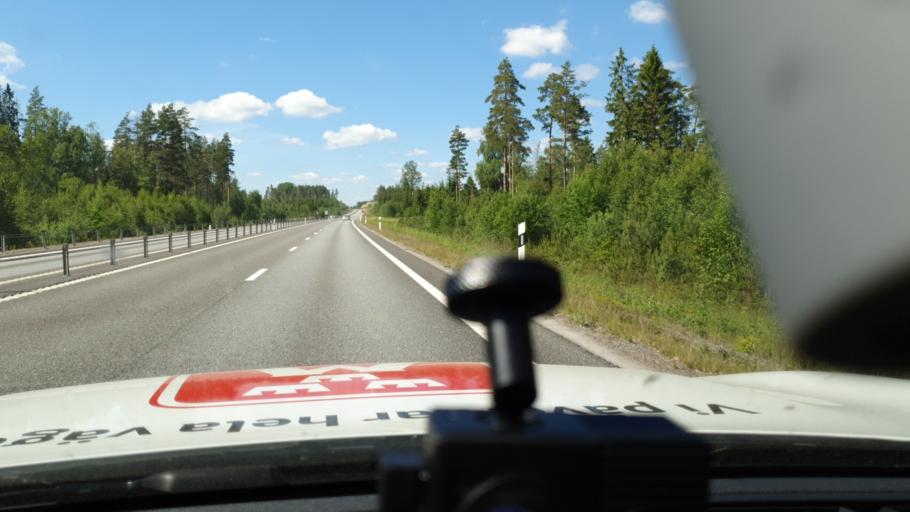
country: SE
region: Kalmar
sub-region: Hultsfreds Kommun
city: Malilla
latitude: 57.3086
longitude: 15.9076
